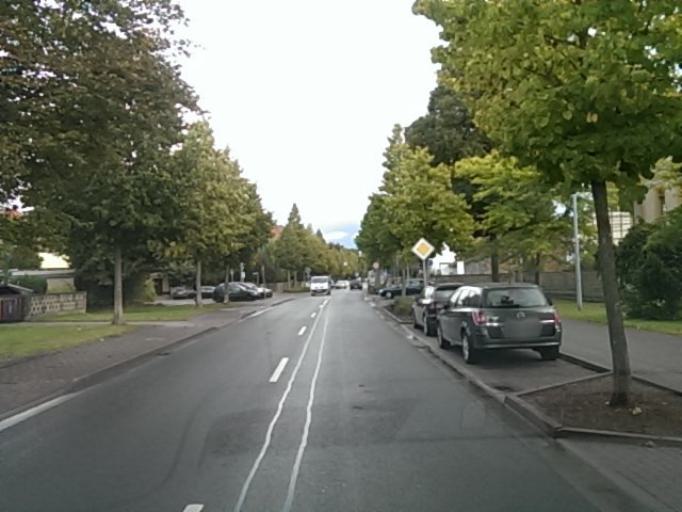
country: DE
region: Thuringia
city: Bad Tennstedt
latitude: 51.1523
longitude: 10.8415
